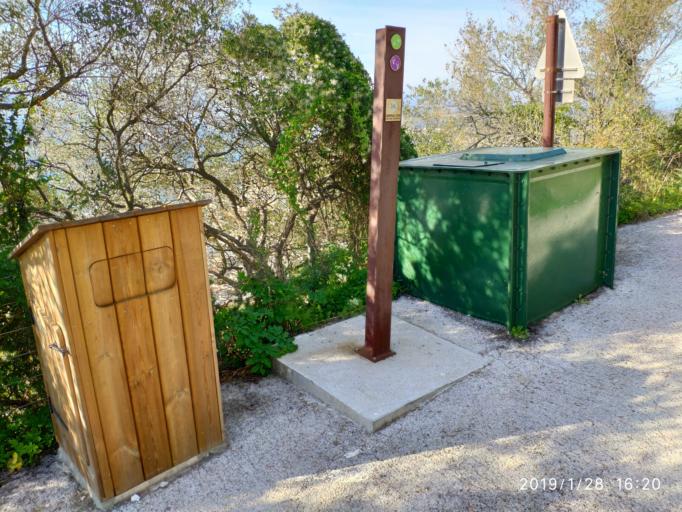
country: GI
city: Gibraltar
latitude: 36.1344
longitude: -5.3475
